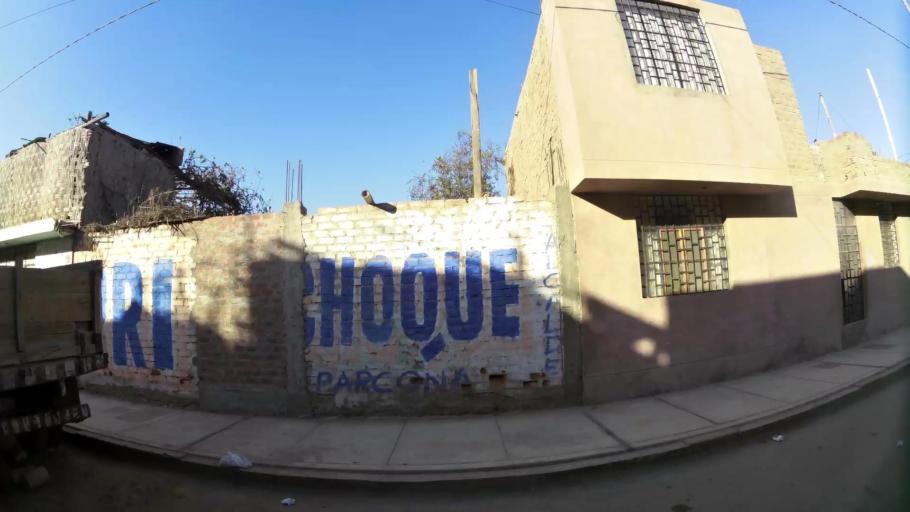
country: PE
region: Ica
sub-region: Provincia de Ica
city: Ica
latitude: -14.0653
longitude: -75.7193
